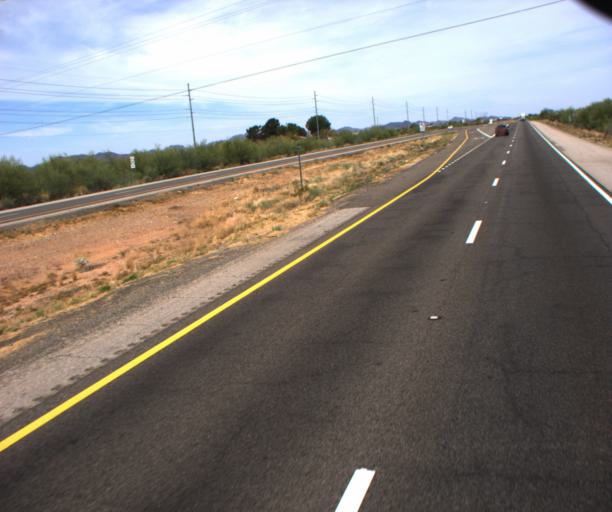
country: US
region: Arizona
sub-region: Maricopa County
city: Wickenburg
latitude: 33.8215
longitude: -112.5844
